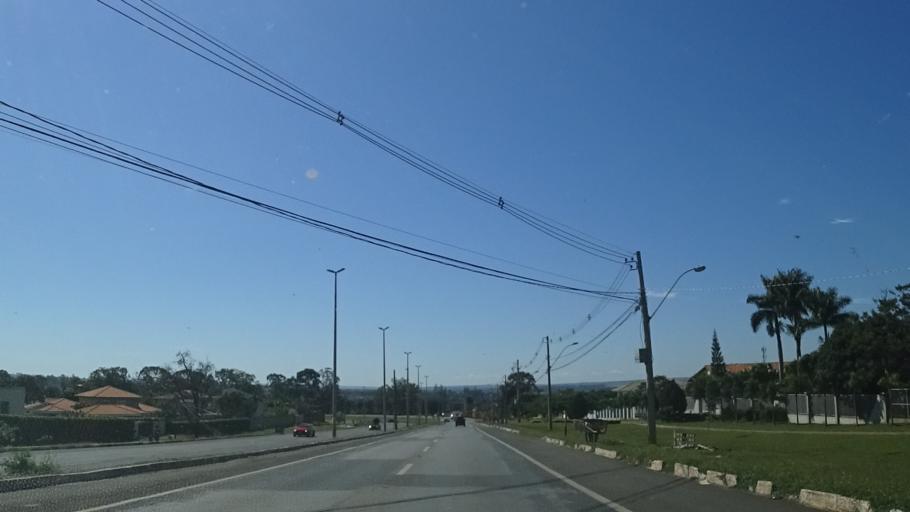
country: BR
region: Federal District
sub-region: Brasilia
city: Brasilia
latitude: -15.8669
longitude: -47.9857
